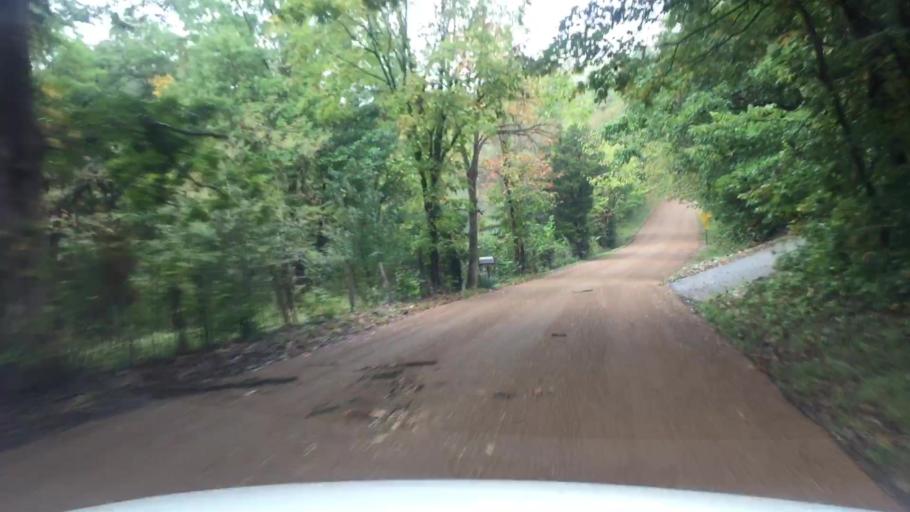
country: US
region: Missouri
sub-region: Boone County
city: Columbia
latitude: 38.8849
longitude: -92.4197
